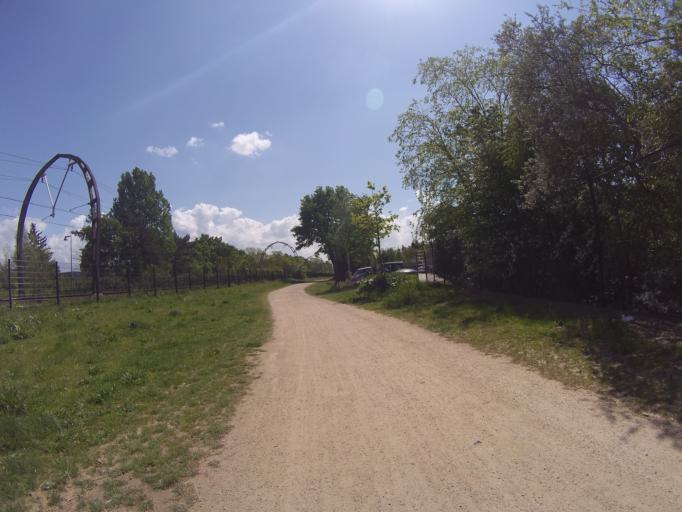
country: NL
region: North Holland
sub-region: Gemeente Hilversum
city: Hilversum
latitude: 52.2135
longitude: 5.1867
